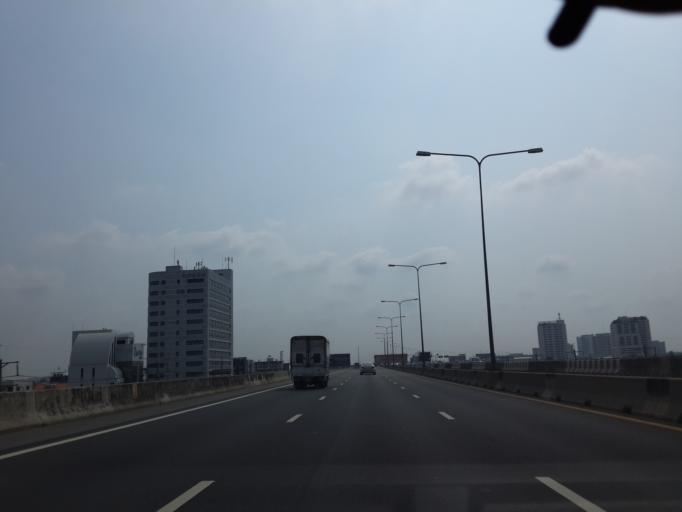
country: TH
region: Bangkok
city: Bang Na
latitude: 13.6640
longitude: 100.6541
